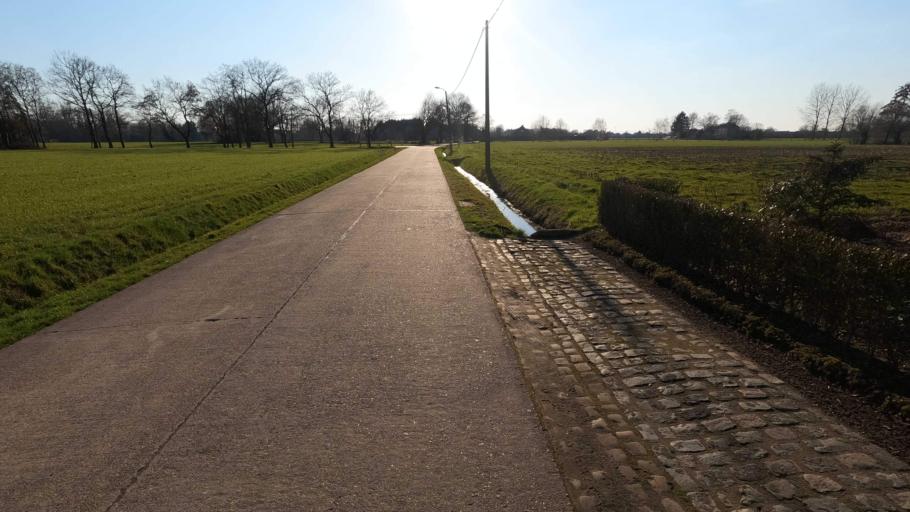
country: BE
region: Flanders
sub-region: Provincie Antwerpen
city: Berlaar
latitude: 51.0882
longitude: 4.6623
